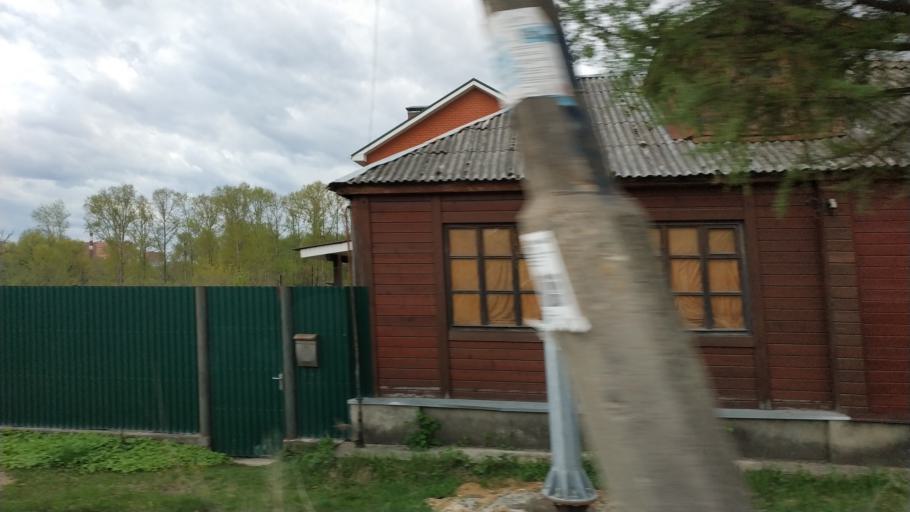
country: RU
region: Moskovskaya
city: Pavlovskiy Posad
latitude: 55.7878
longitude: 38.6860
